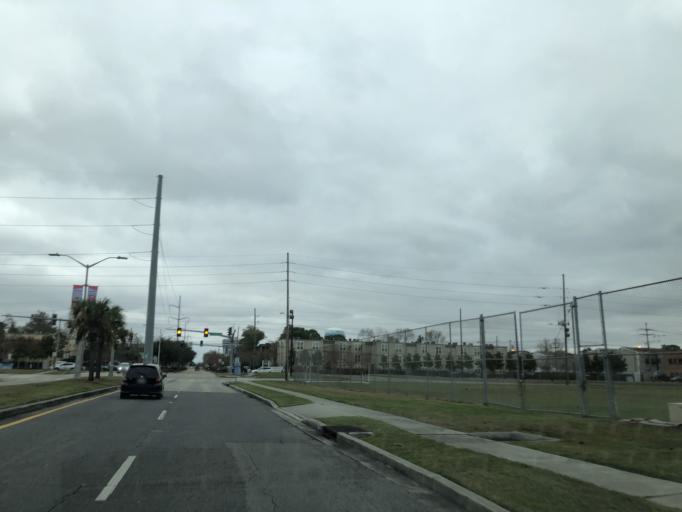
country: US
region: Louisiana
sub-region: Jefferson Parish
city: Metairie
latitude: 29.9915
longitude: -90.1600
